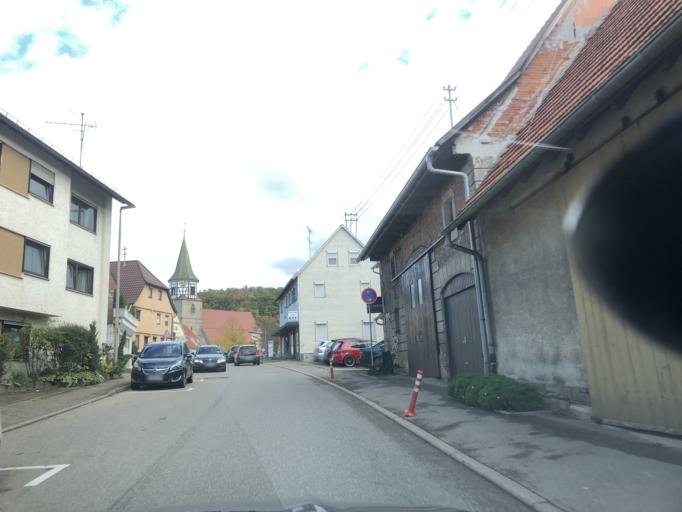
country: DE
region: Baden-Wuerttemberg
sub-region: Regierungsbezirk Stuttgart
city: Allmersbach im Tal
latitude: 48.8594
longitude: 9.4674
